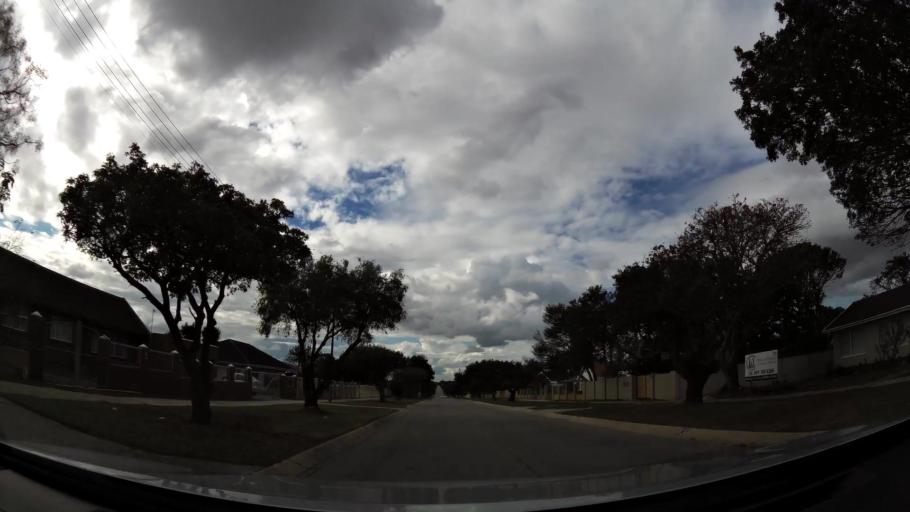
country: ZA
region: Eastern Cape
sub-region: Nelson Mandela Bay Metropolitan Municipality
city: Port Elizabeth
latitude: -33.9426
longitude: 25.5187
